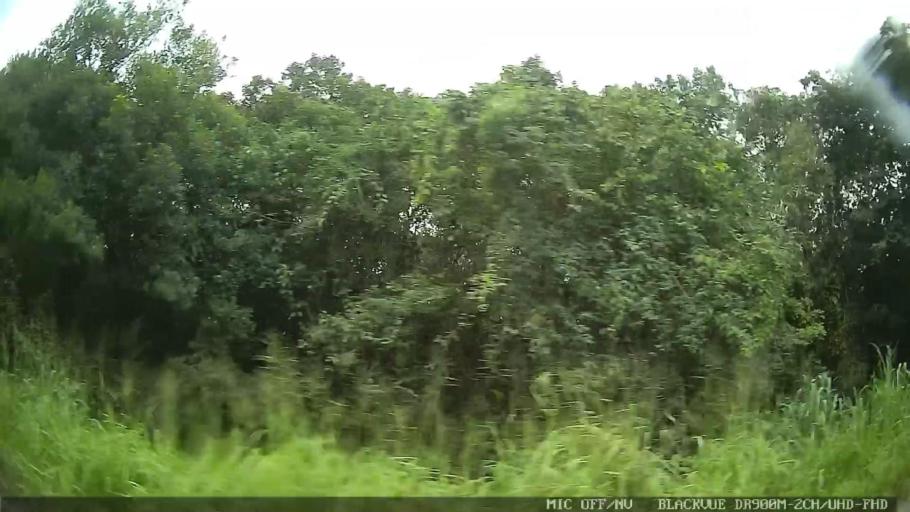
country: BR
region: Sao Paulo
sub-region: Itanhaem
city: Itanhaem
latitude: -24.1464
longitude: -46.7773
